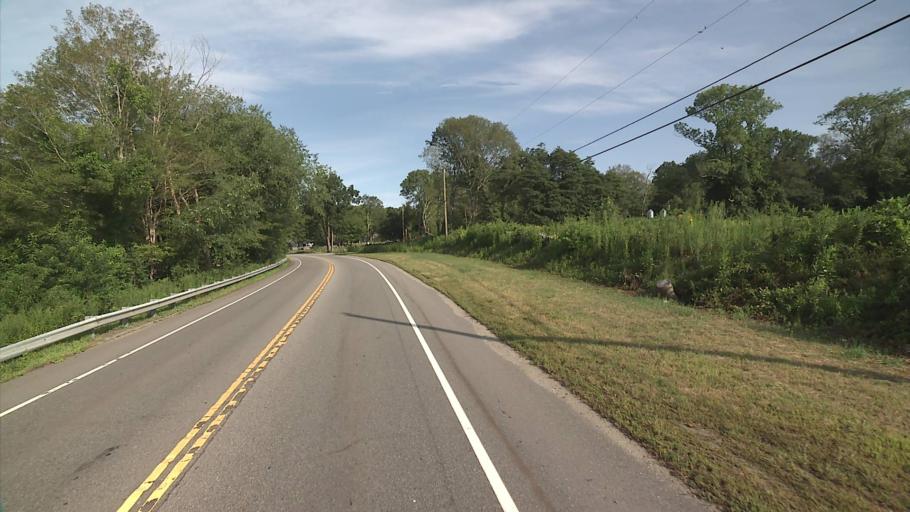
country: US
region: Connecticut
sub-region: New London County
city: Preston City
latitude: 41.4663
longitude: -71.9116
